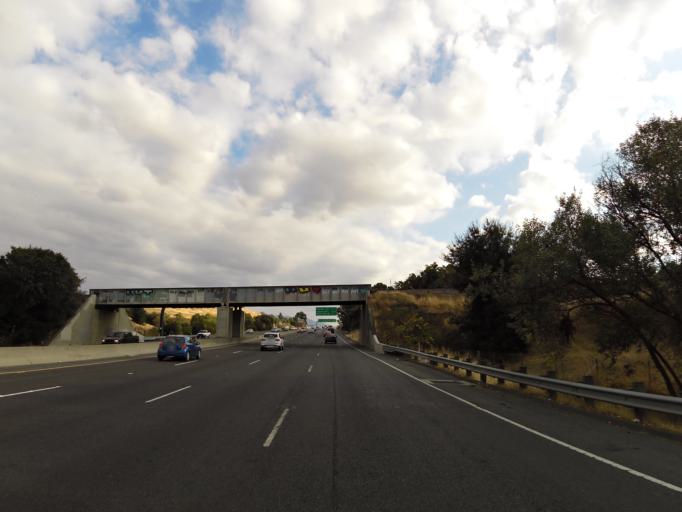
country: US
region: California
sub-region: Contra Costa County
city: Vine Hill
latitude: 38.0058
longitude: -122.0830
